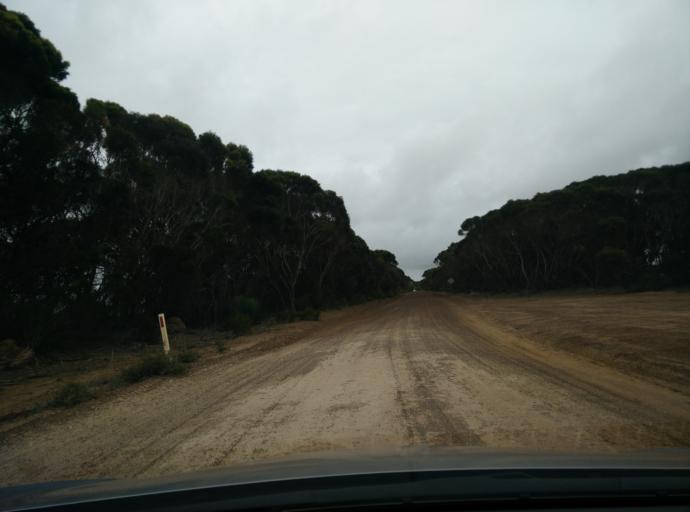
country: AU
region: South Australia
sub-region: Kangaroo Island
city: Kingscote
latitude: -35.8523
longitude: 137.4825
